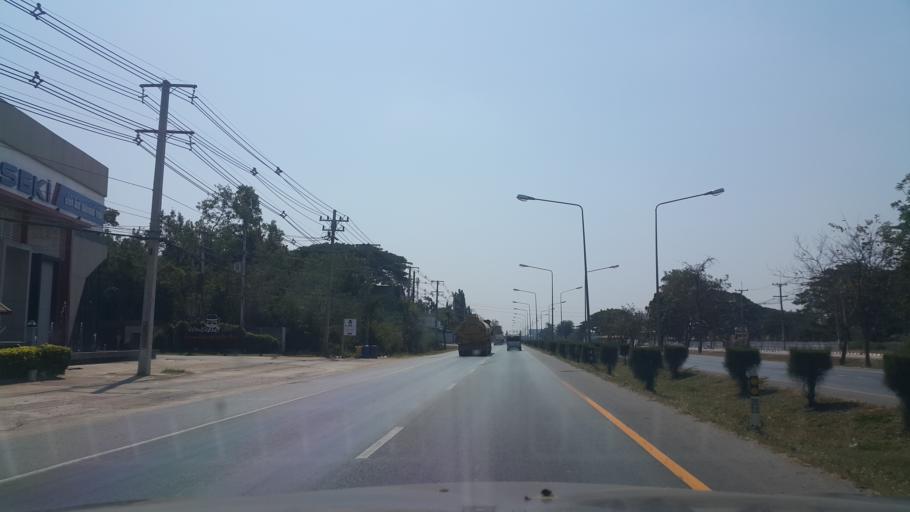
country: TH
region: Khon Kaen
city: Ban Phai
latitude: 16.0758
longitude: 102.7233
